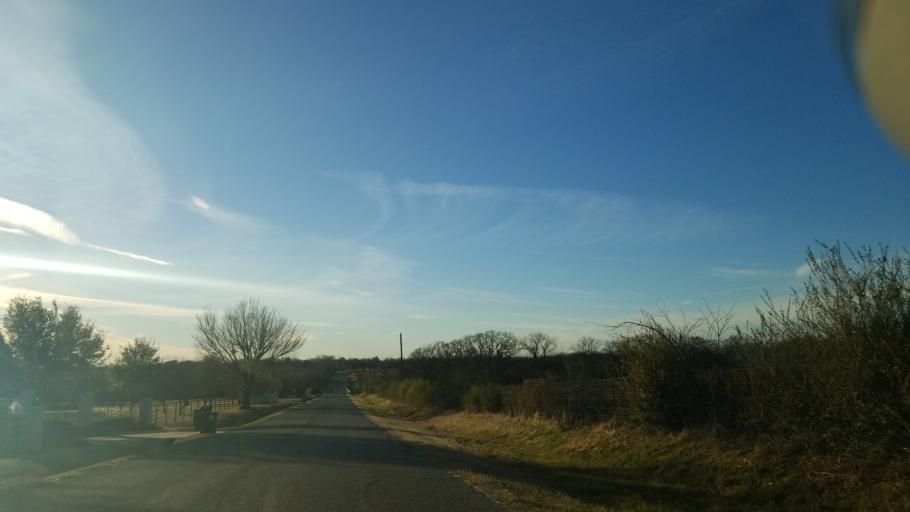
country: US
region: Texas
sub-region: Denton County
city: Denton
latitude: 33.1833
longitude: -97.1483
